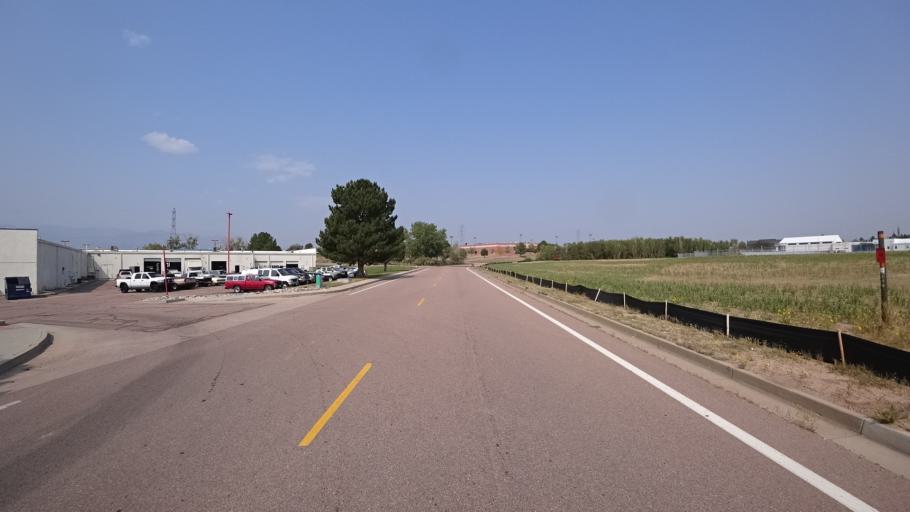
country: US
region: Colorado
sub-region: El Paso County
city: Stratmoor
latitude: 38.8080
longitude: -104.7548
